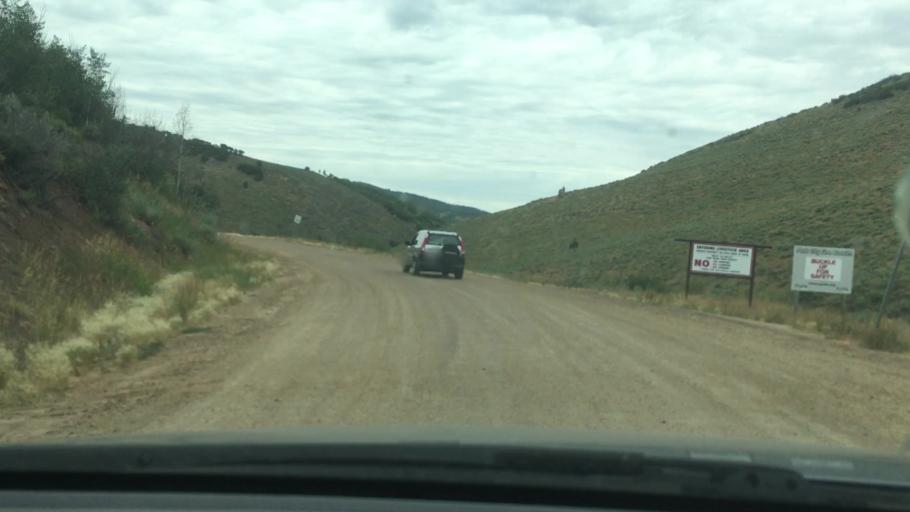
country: US
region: Utah
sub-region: Summit County
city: Summit Park
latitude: 40.7695
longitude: -111.5842
